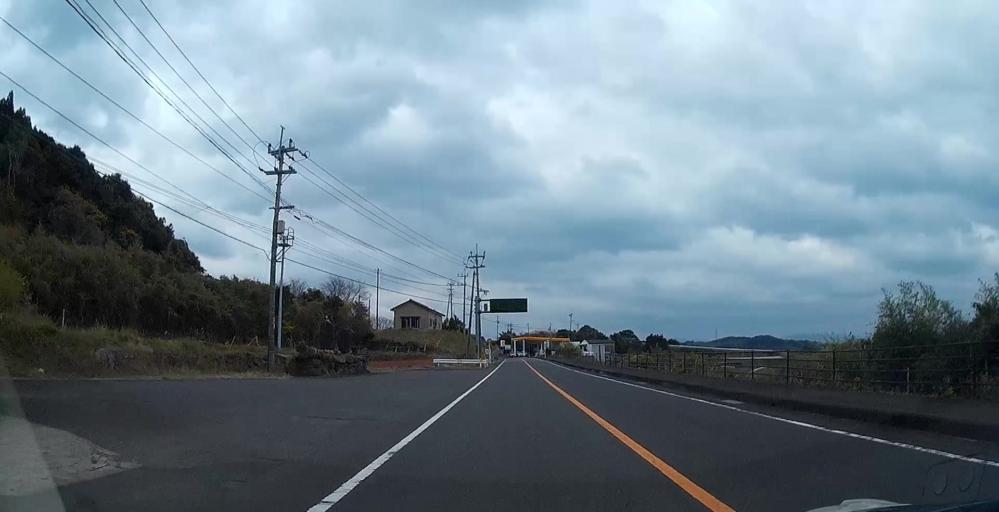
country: JP
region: Kagoshima
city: Akune
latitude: 32.0966
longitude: 130.1632
